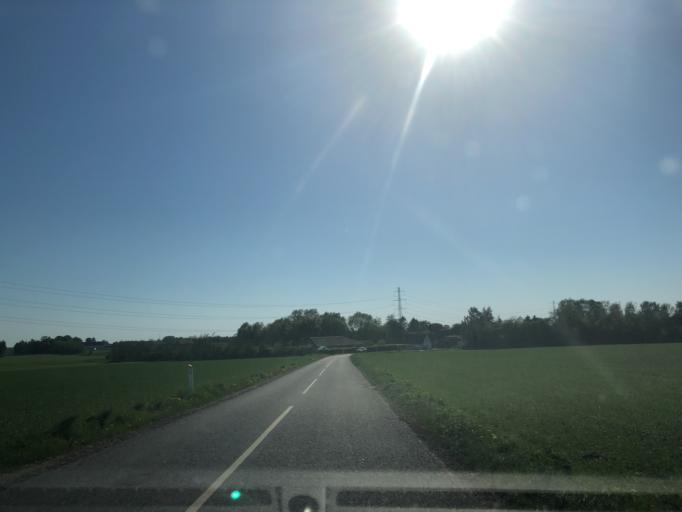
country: DK
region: Zealand
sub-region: Ringsted Kommune
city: Ringsted
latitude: 55.4683
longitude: 11.6928
